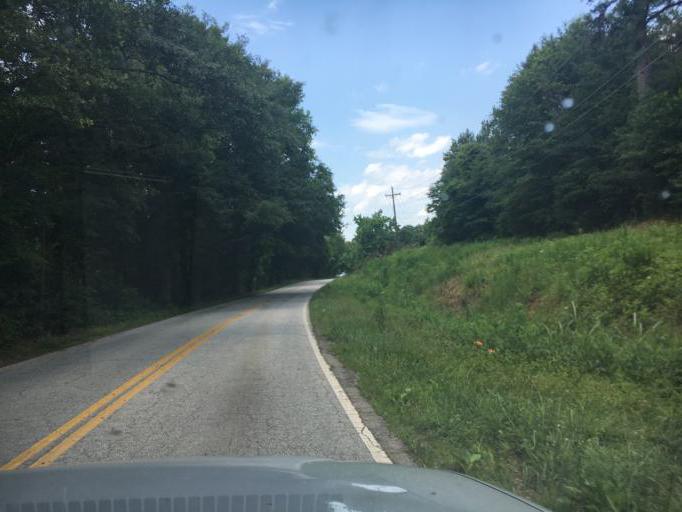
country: US
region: South Carolina
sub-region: Greenville County
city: Five Forks
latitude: 34.8701
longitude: -82.2444
